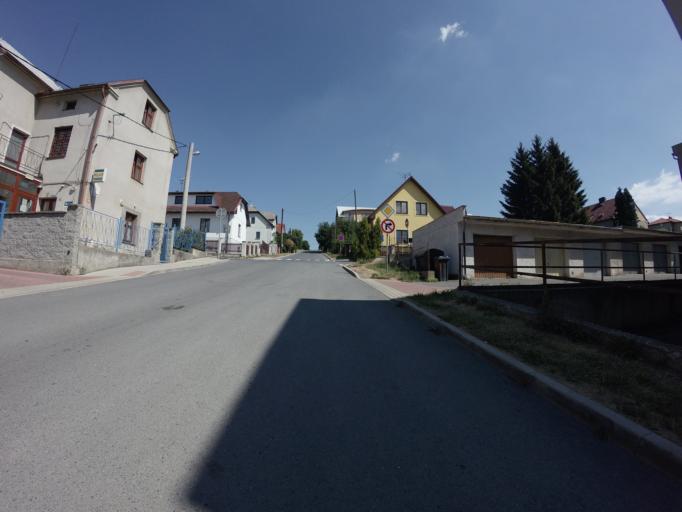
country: CZ
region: Central Bohemia
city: Jilove u Prahy
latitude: 49.8967
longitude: 14.4891
